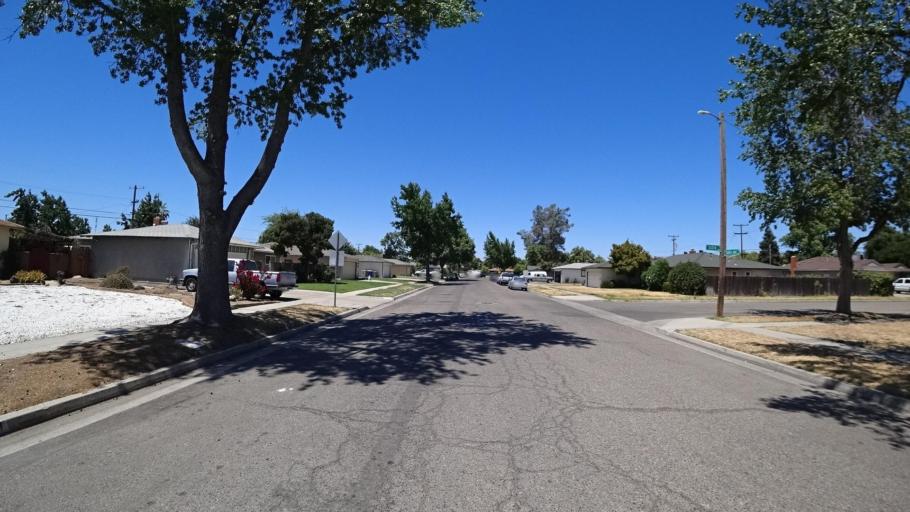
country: US
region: California
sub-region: Fresno County
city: Fresno
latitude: 36.8046
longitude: -119.7631
